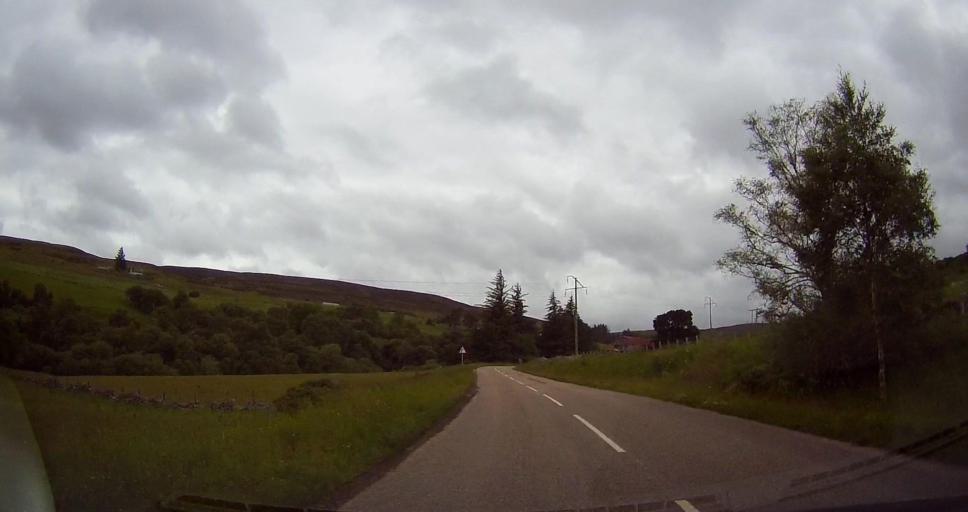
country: GB
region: Scotland
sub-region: Highland
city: Dornoch
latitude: 58.0065
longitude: -4.2498
